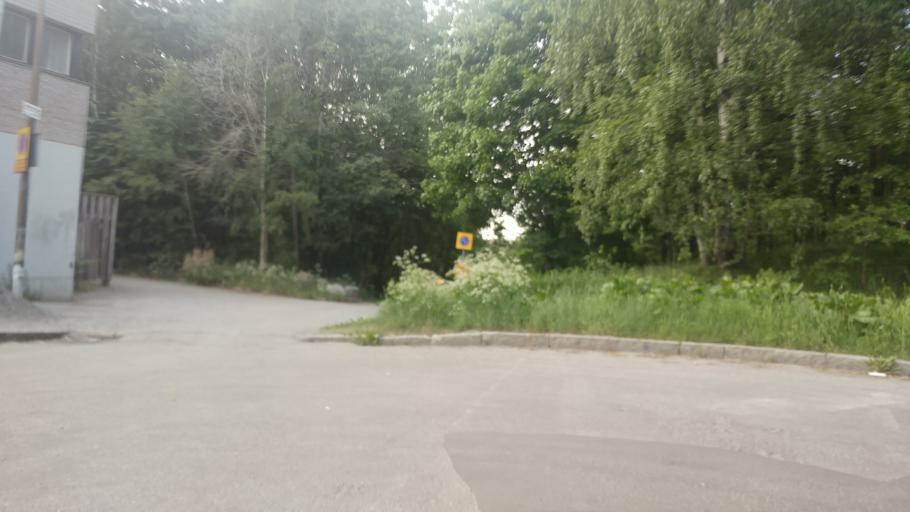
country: SE
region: Stockholm
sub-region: Danderyds Kommun
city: Djursholm
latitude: 59.3712
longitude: 18.0682
